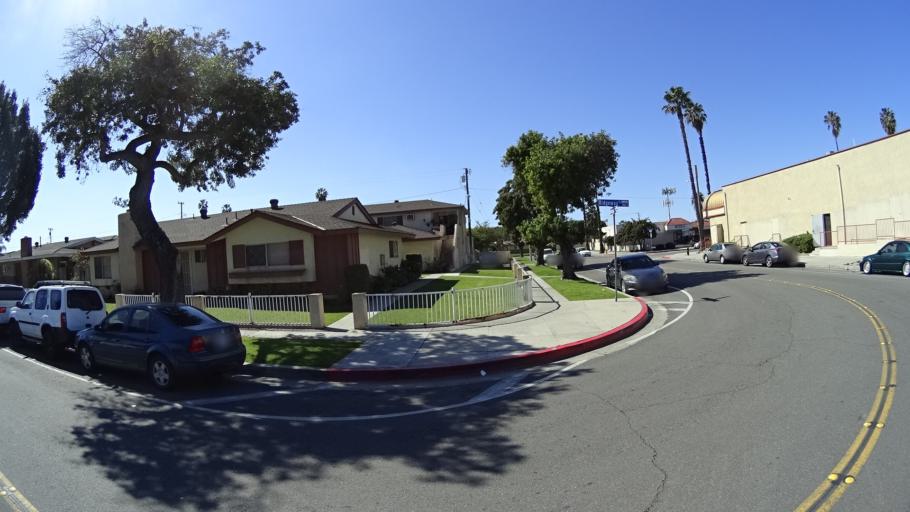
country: US
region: California
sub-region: Orange County
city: Stanton
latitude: 33.8310
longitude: -117.9908
